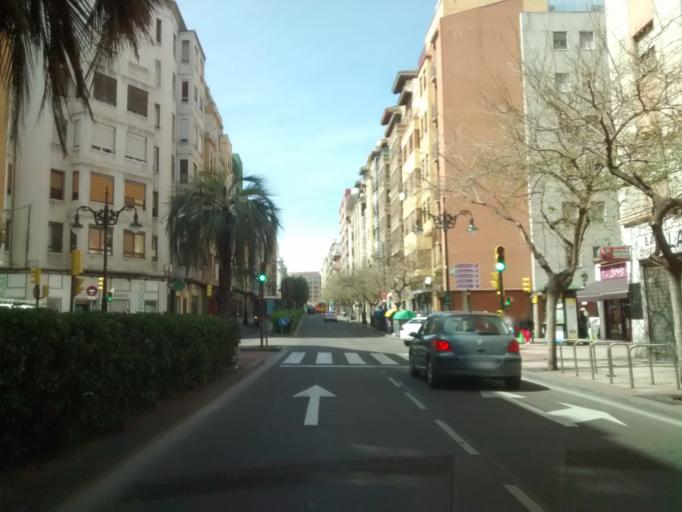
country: ES
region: Aragon
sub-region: Provincia de Zaragoza
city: Zaragoza
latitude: 41.6553
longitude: -0.8890
